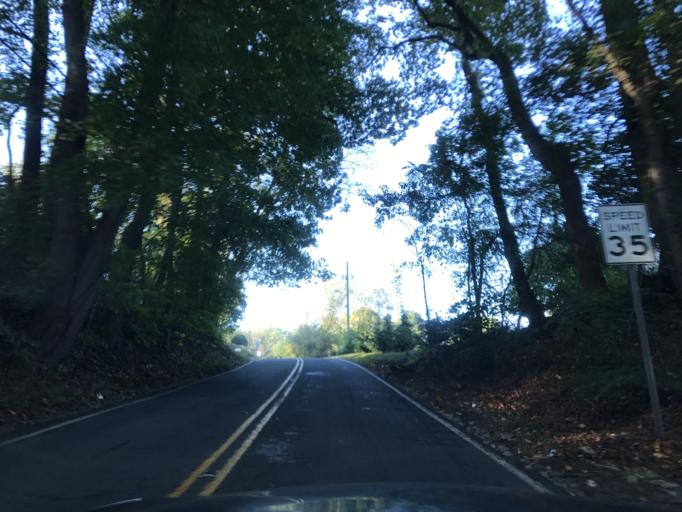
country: US
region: Maryland
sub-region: Anne Arundel County
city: Gambrills
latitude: 39.0284
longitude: -76.6505
